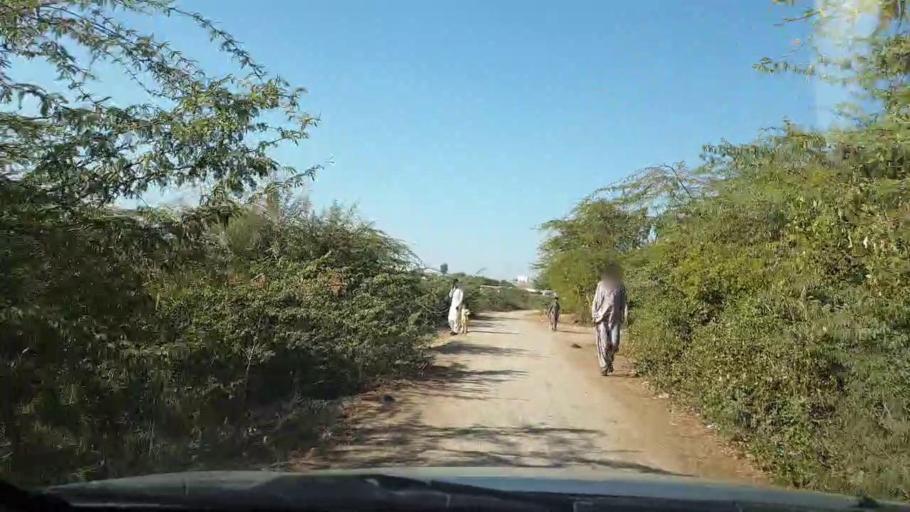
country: PK
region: Sindh
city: Berani
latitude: 25.8186
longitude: 68.9424
